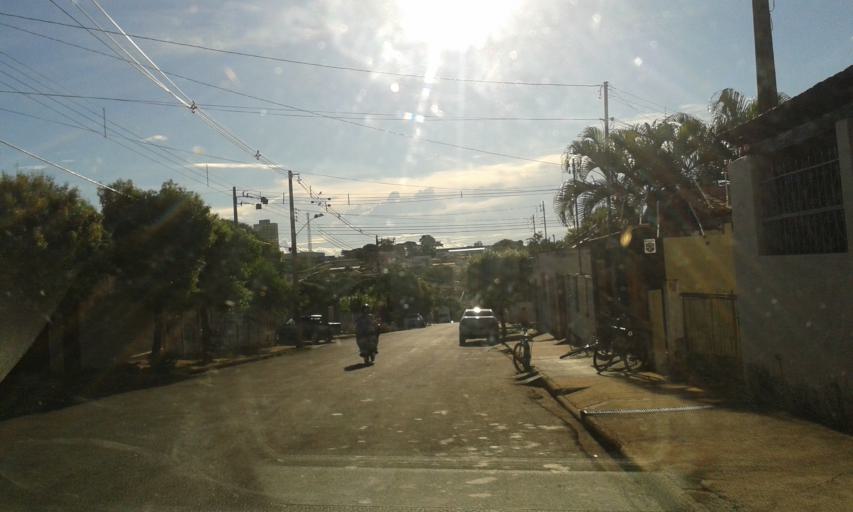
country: BR
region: Minas Gerais
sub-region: Ituiutaba
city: Ituiutaba
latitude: -18.9648
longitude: -49.4578
